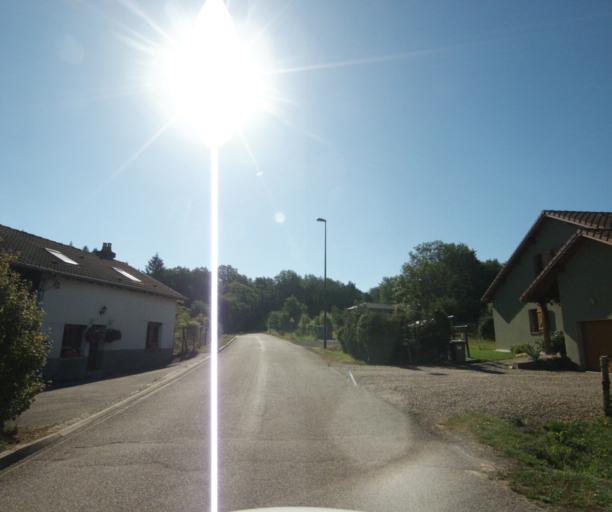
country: FR
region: Lorraine
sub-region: Departement des Vosges
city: Archettes
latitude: 48.1646
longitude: 6.5406
